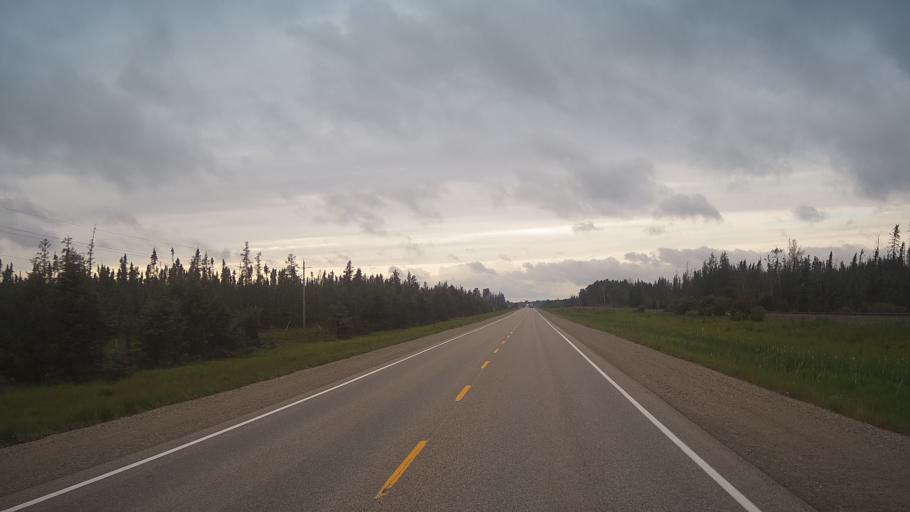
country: CA
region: Ontario
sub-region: Thunder Bay District
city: Thunder Bay
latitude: 48.8637
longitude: -89.9672
